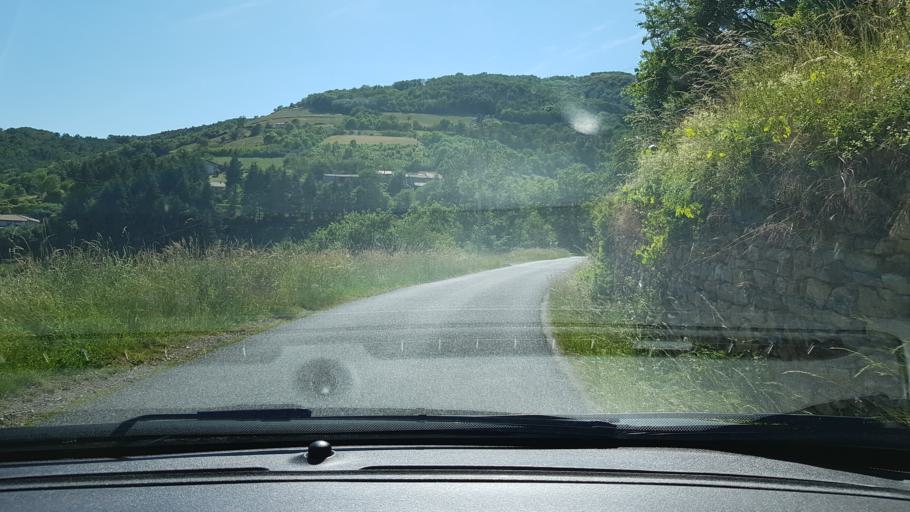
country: FR
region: Rhone-Alpes
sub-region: Departement du Rhone
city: Saint-Didier-sous-Riverie
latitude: 45.5890
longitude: 4.5946
